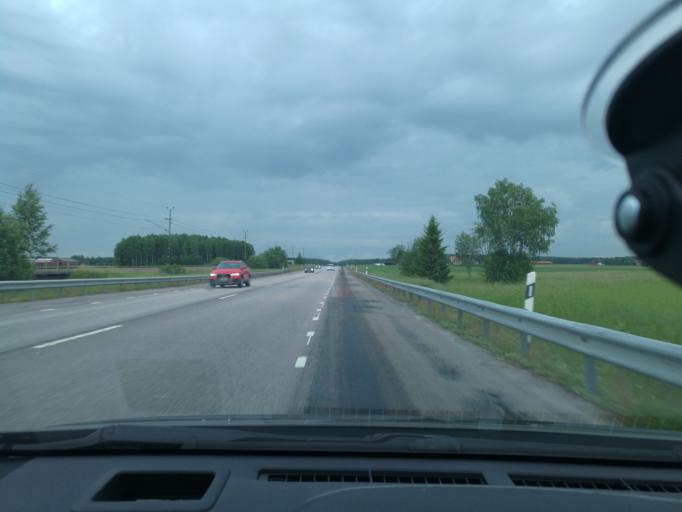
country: SE
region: Vaestmanland
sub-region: Sala Kommun
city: Sala
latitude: 59.9260
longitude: 16.6713
